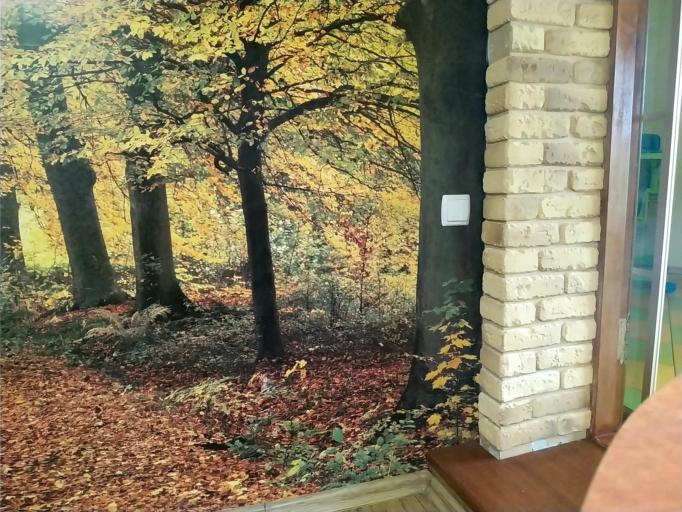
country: RU
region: Smolensk
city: Dorogobuzh
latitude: 54.8248
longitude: 33.3439
